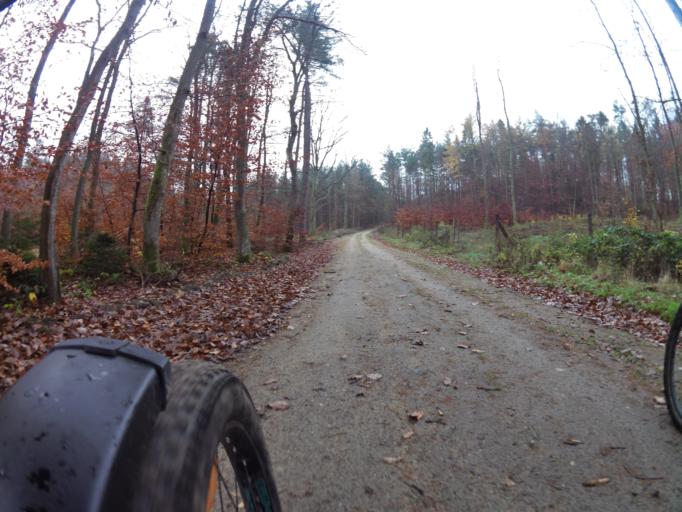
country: PL
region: Pomeranian Voivodeship
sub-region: Powiat pucki
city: Krokowa
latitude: 54.7788
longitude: 18.0918
